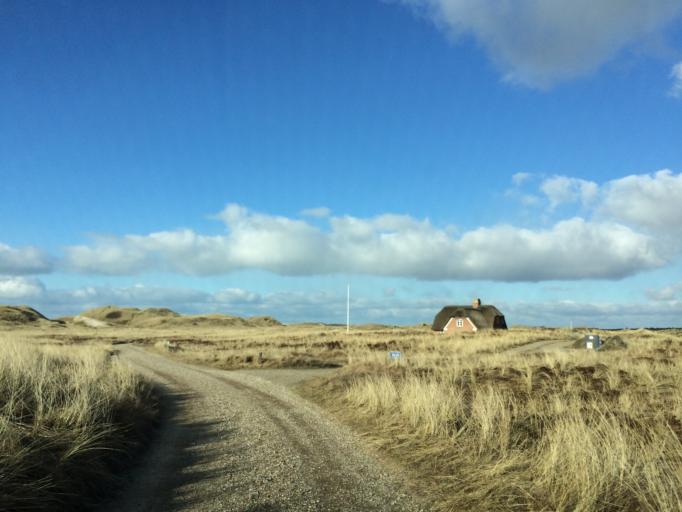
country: DK
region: Central Jutland
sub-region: Holstebro Kommune
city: Ulfborg
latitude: 56.2719
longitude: 8.1349
